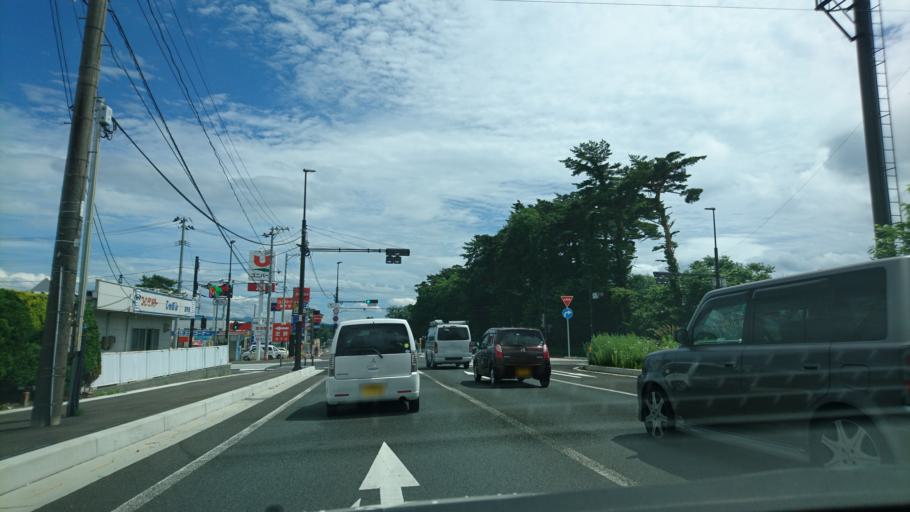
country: JP
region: Iwate
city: Morioka-shi
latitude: 39.7745
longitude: 141.1276
